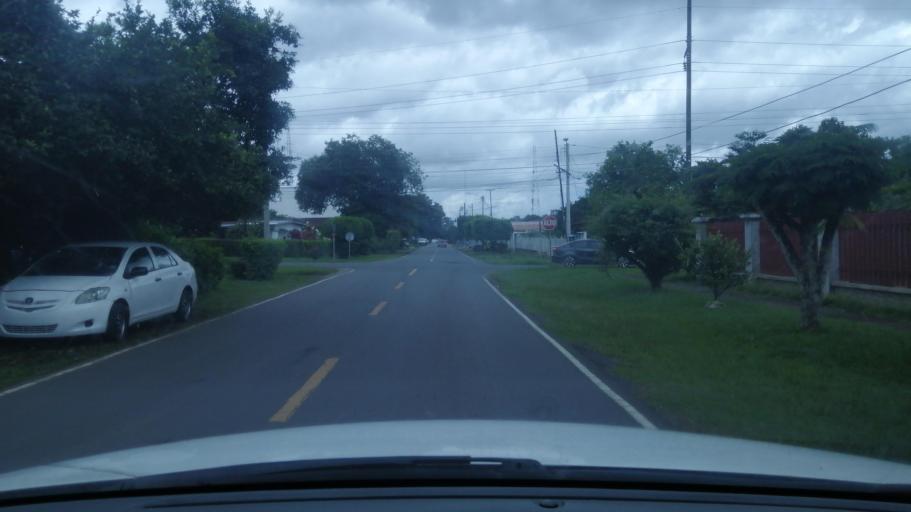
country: PA
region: Chiriqui
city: David
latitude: 8.4444
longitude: -82.4275
